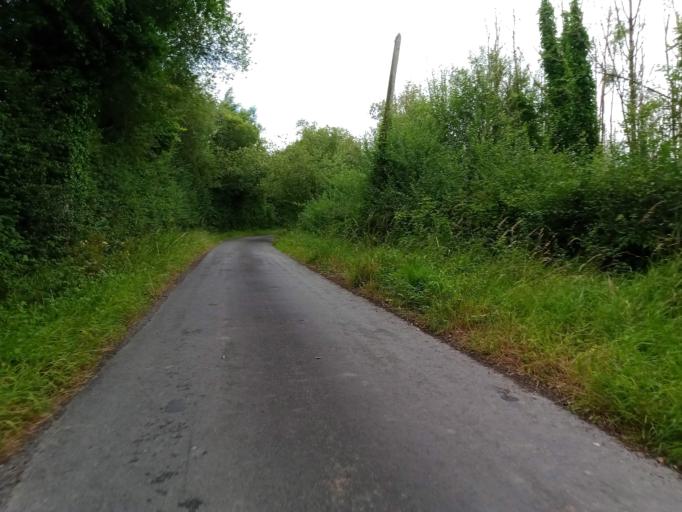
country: IE
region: Leinster
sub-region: Kilkenny
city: Callan
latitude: 52.5769
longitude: -7.4055
